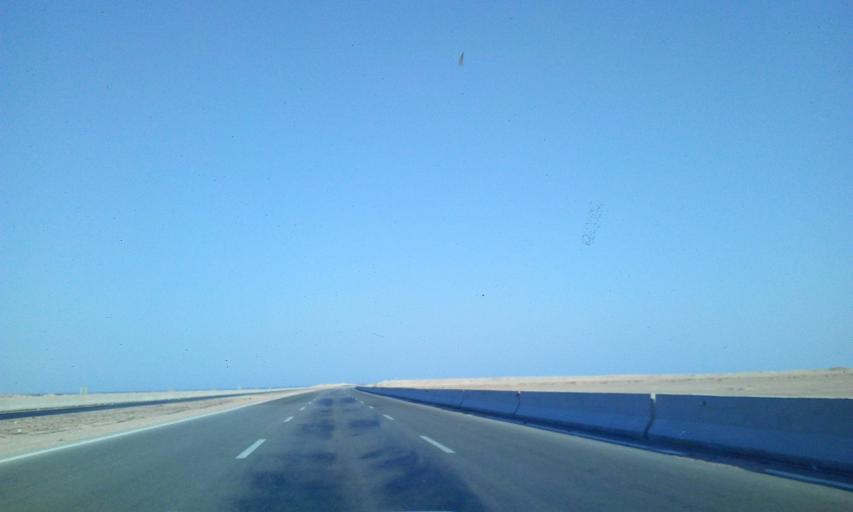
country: EG
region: As Suways
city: Ain Sukhna
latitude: 29.1025
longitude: 32.6167
